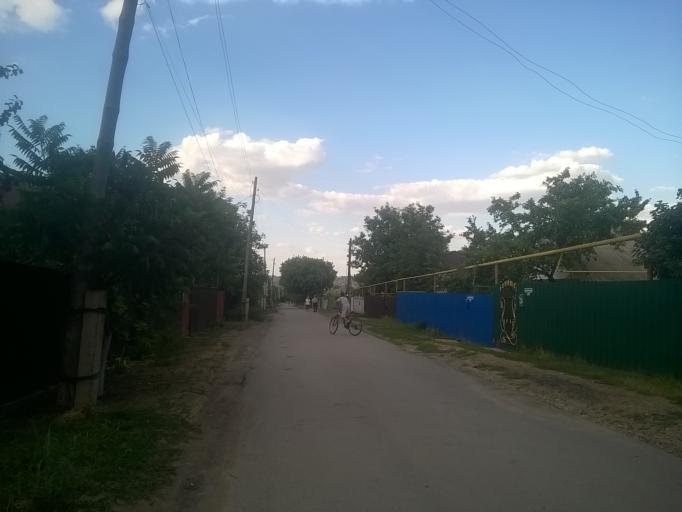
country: RU
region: Rostov
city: Donetsk
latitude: 48.3385
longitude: 39.9570
